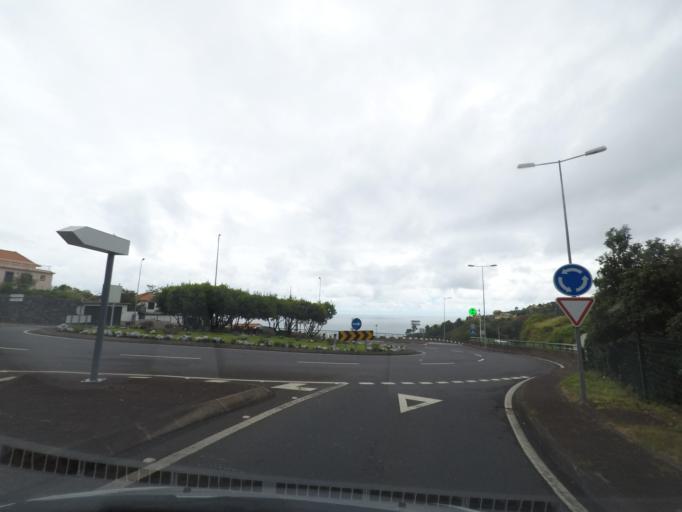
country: PT
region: Madeira
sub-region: Santana
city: Santana
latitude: 32.7924
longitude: -16.8519
